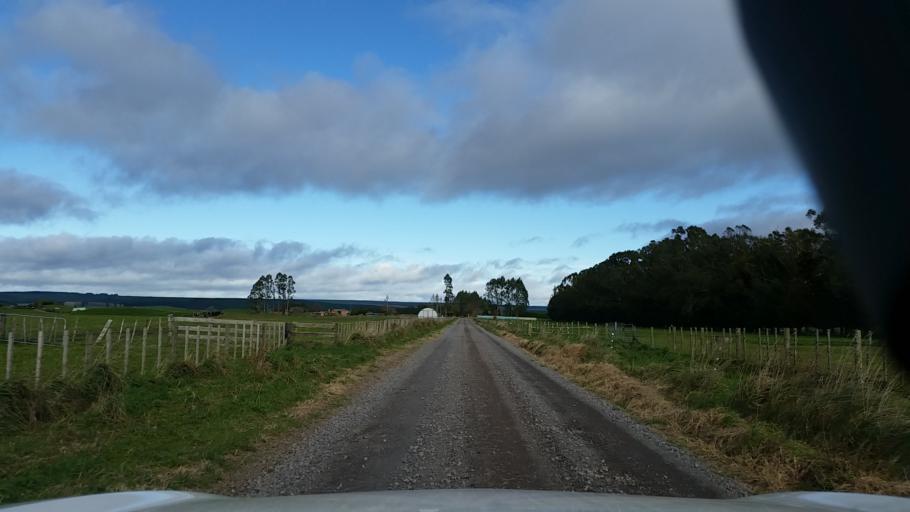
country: NZ
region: Bay of Plenty
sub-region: Whakatane District
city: Murupara
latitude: -38.4746
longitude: 176.4158
